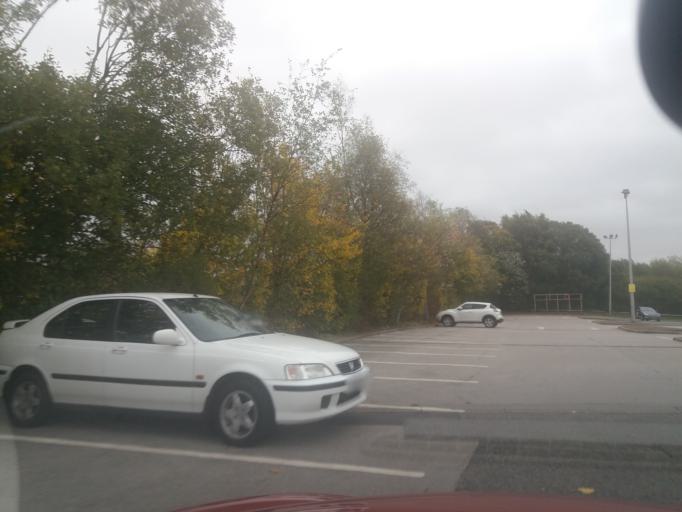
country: GB
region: England
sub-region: Lancashire
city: Chorley
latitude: 53.6483
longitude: -2.6239
